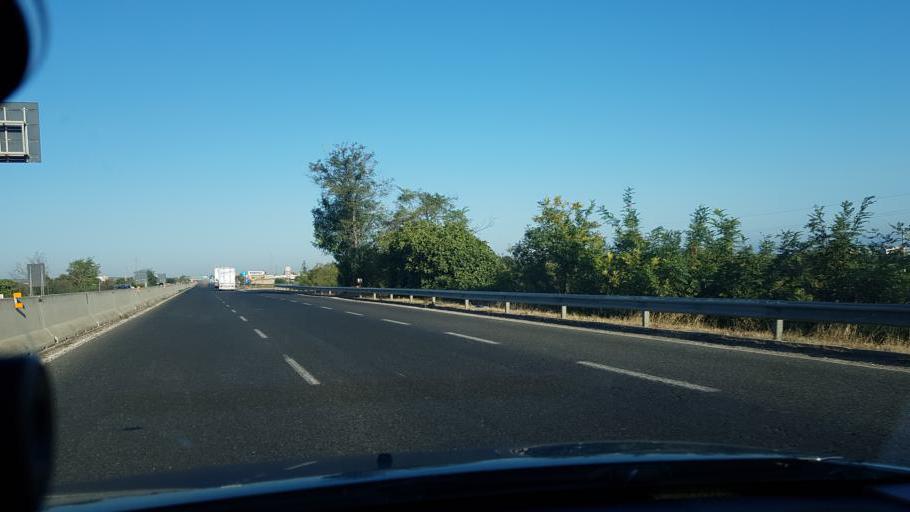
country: IT
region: Apulia
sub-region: Provincia di Bari
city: Monopoli
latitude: 40.9411
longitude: 17.2822
